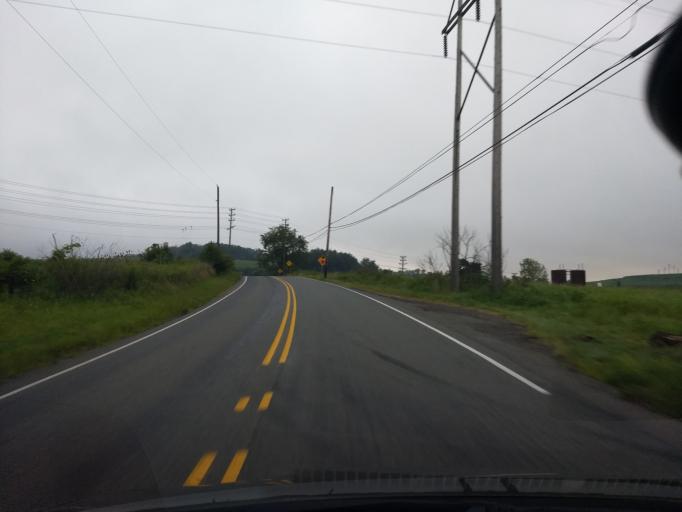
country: US
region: Pennsylvania
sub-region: Westmoreland County
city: Greensburg
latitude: 40.3269
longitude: -79.4886
